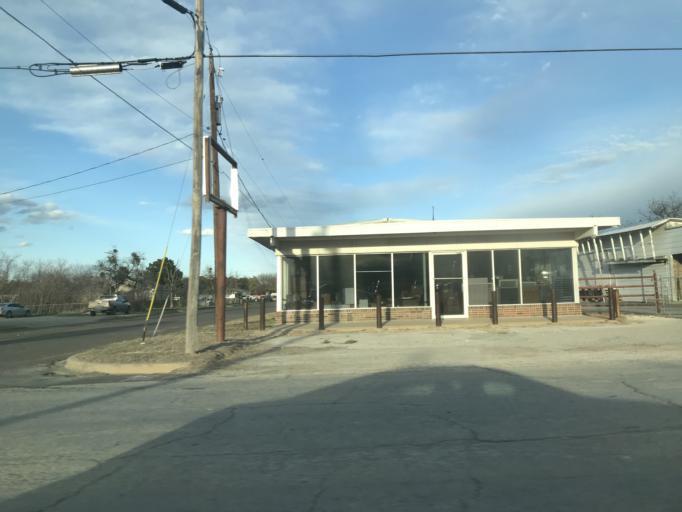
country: US
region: Texas
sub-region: Tom Green County
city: San Angelo
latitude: 31.4942
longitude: -100.4573
